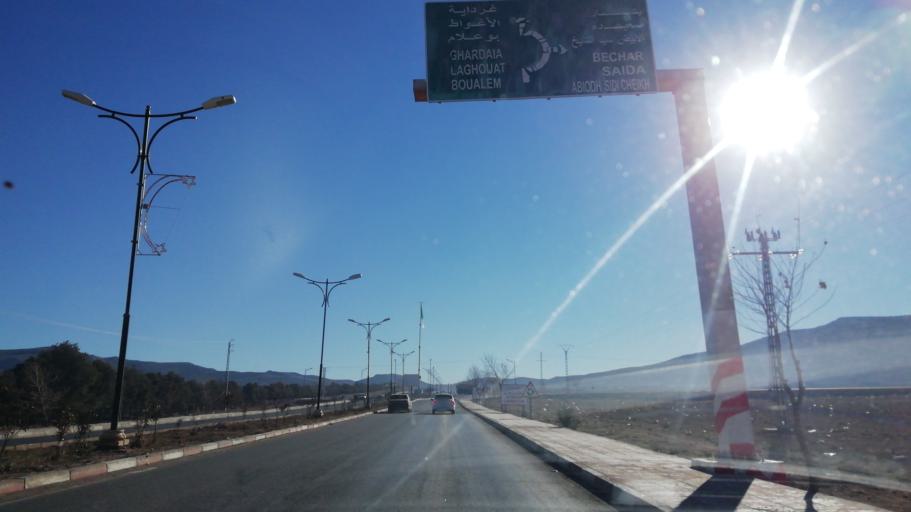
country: DZ
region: El Bayadh
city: El Bayadh
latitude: 33.6619
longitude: 1.0549
